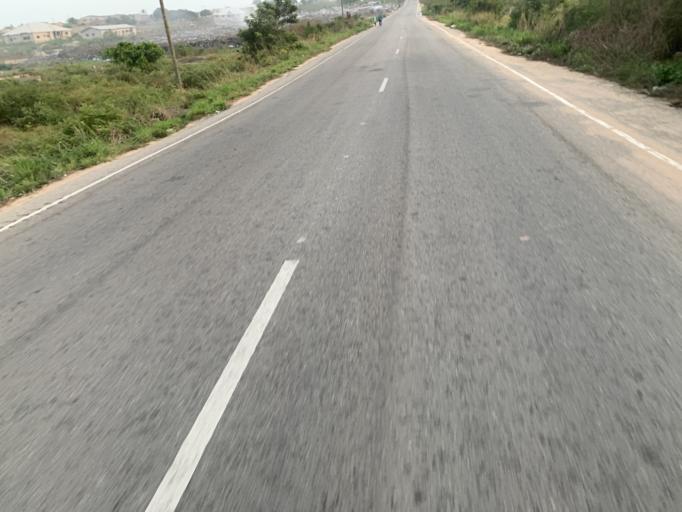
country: GH
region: Central
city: Winneba
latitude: 5.3644
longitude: -0.6087
